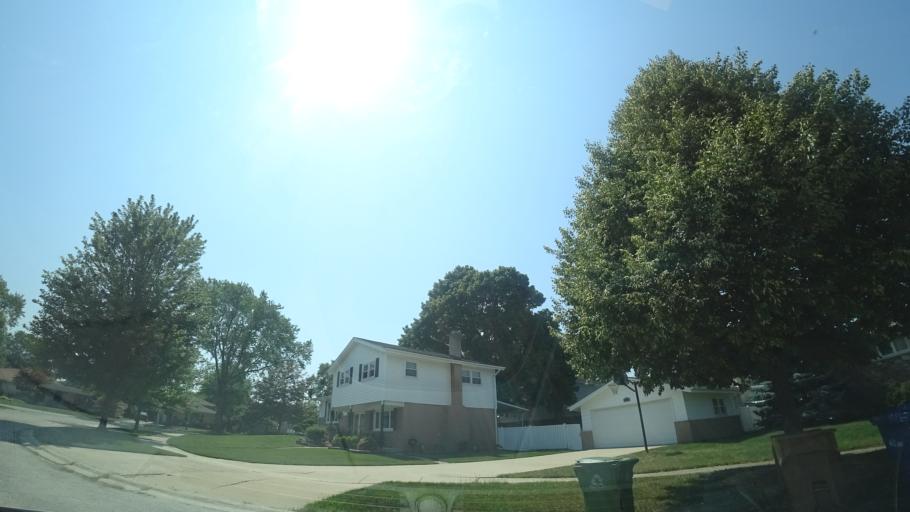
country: US
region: Illinois
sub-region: Cook County
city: Oak Lawn
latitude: 41.7000
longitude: -87.7512
